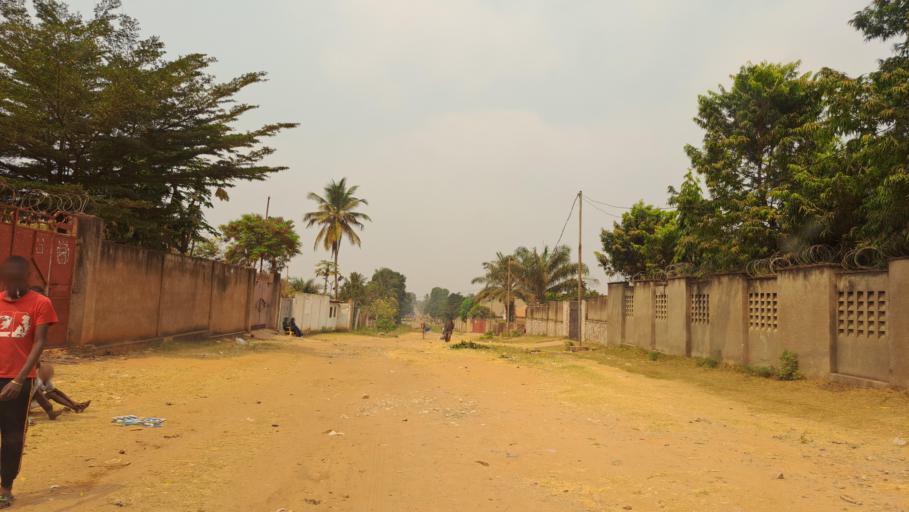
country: CD
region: Kasai-Oriental
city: Mbuji-Mayi
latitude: -6.1097
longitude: 23.5971
